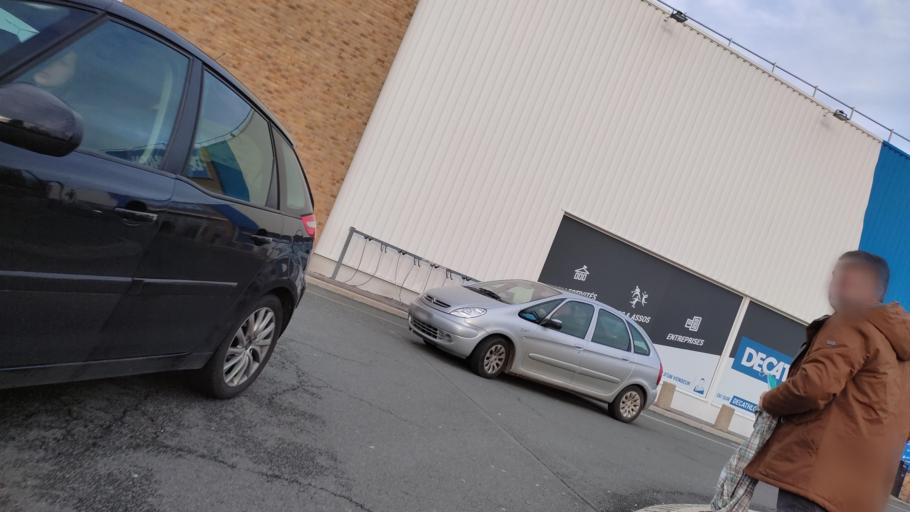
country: FR
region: Nord-Pas-de-Calais
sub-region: Departement du Pas-de-Calais
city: Anzin-Saint-Aubin
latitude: 50.3029
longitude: 2.7303
